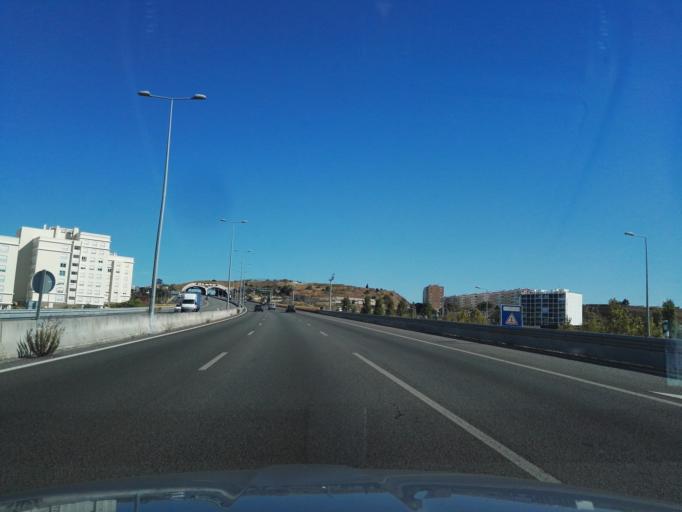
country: PT
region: Lisbon
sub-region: Odivelas
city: Olival do Basto
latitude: 38.7800
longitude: -9.1562
